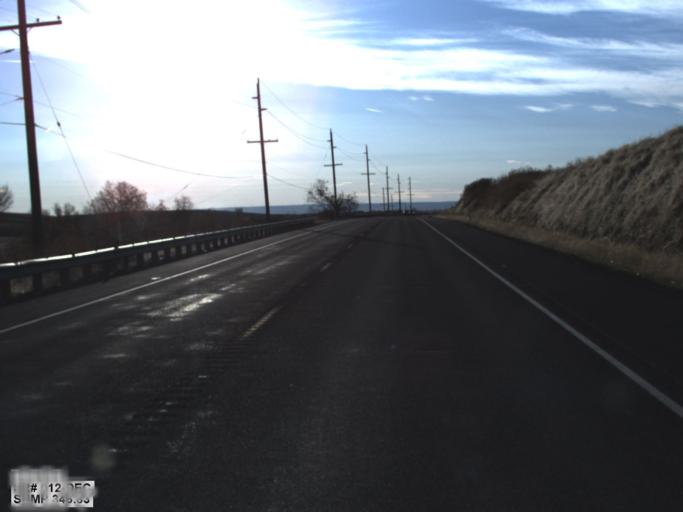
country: US
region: Washington
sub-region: Walla Walla County
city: Waitsburg
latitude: 46.1342
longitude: -118.1741
